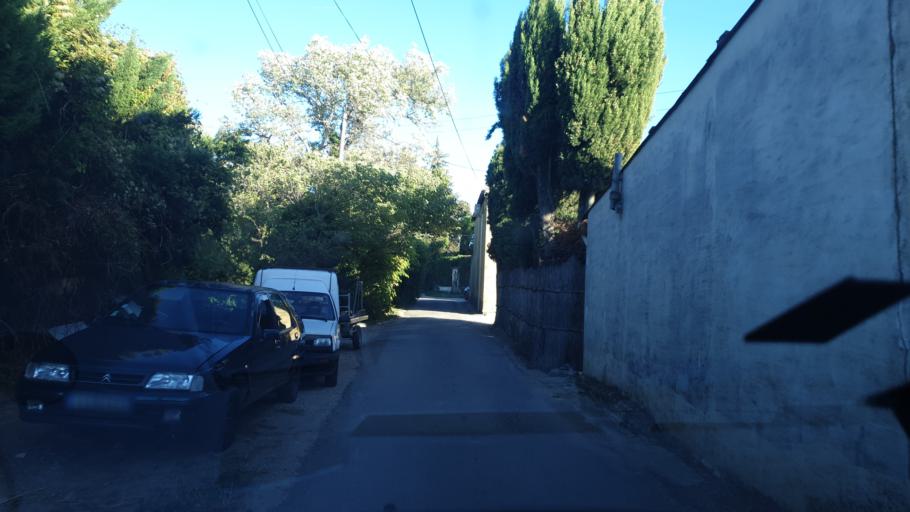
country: FR
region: Provence-Alpes-Cote d'Azur
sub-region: Departement du Vaucluse
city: Loriol-du-Comtat
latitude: 44.0586
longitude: 5.0167
